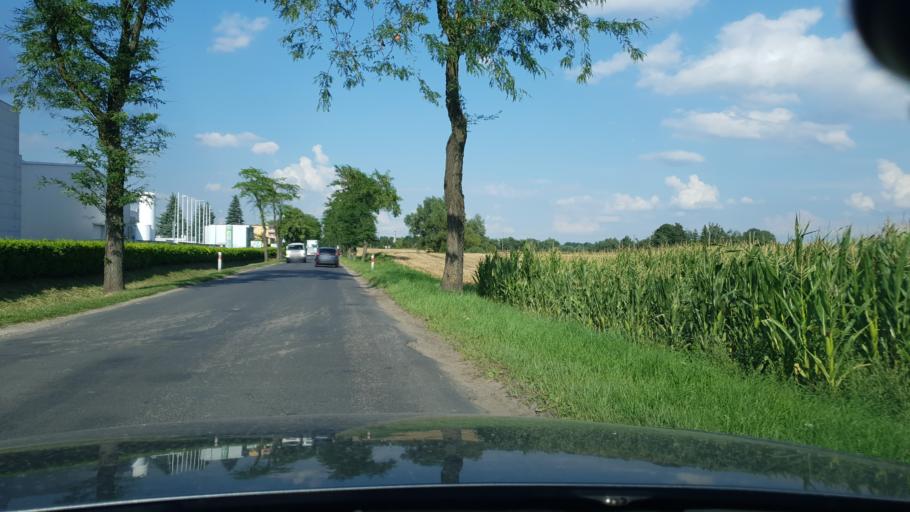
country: PL
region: Kujawsko-Pomorskie
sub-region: Powiat wabrzeski
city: Wabrzezno
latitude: 53.2740
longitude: 18.9205
